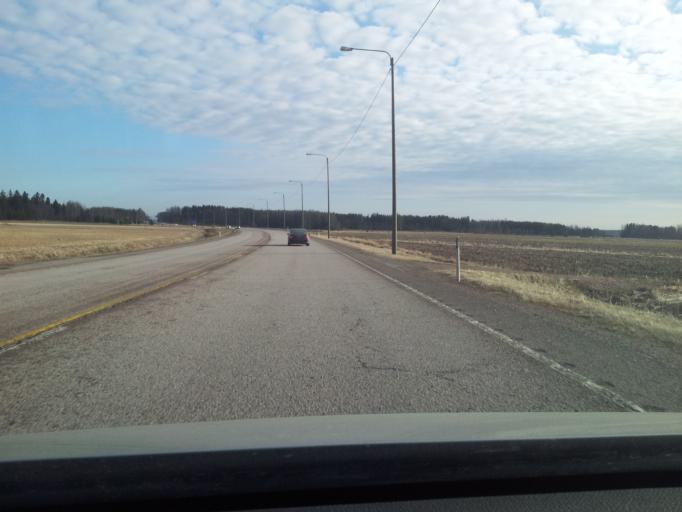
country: FI
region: Uusimaa
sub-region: Loviisa
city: Lapinjaervi
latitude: 60.6277
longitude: 26.2240
